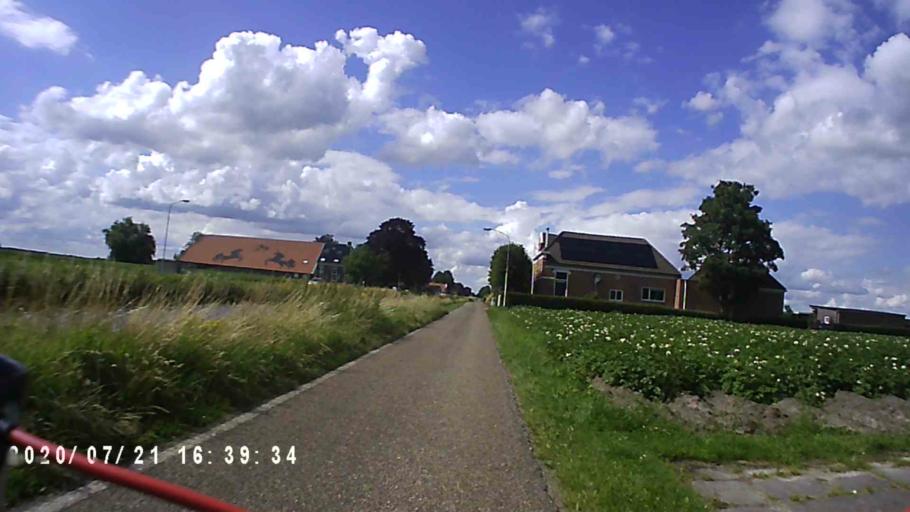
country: NL
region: Groningen
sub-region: Gemeente Hoogezand-Sappemeer
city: Sappemeer
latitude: 53.0957
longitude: 6.7920
